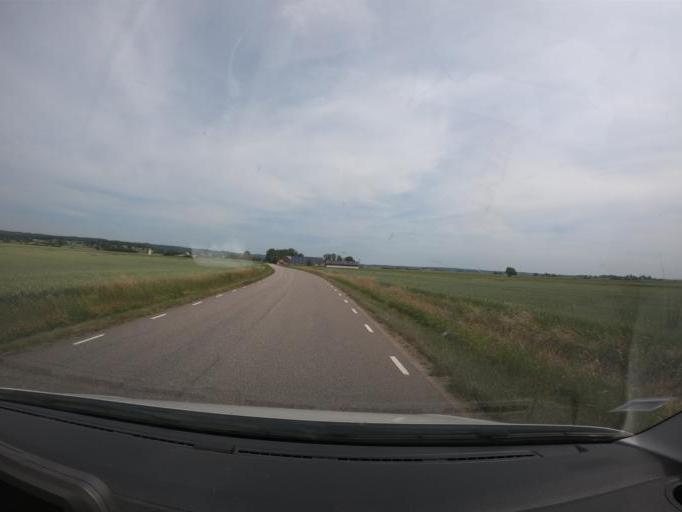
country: SE
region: Skane
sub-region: Bastads Kommun
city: Forslov
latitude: 56.3190
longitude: 12.8173
